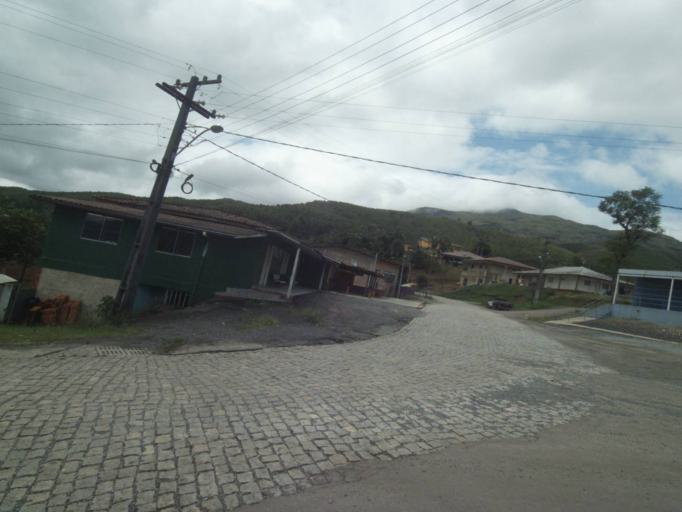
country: BR
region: Parana
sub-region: Campina Grande Do Sul
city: Campina Grande do Sul
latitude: -25.1079
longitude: -48.8077
